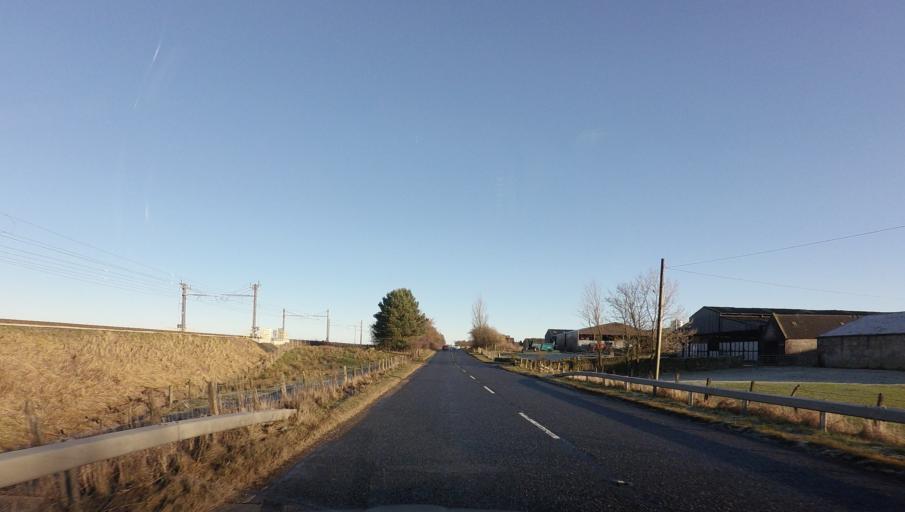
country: GB
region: Scotland
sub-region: West Lothian
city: Fauldhouse
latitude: 55.8219
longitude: -3.6848
